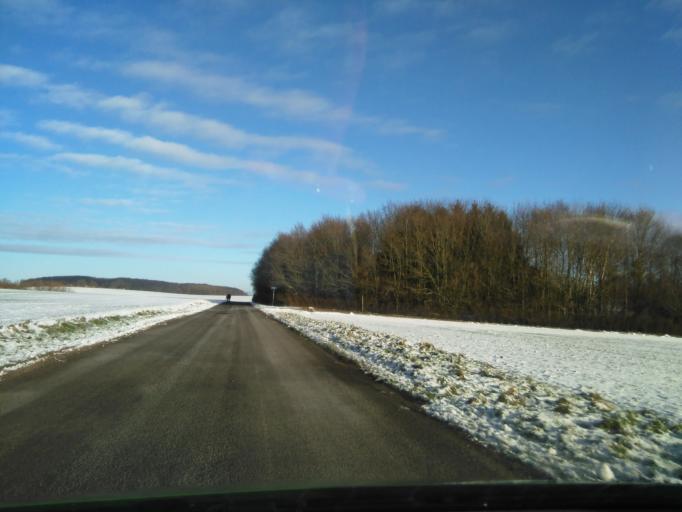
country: DK
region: Central Jutland
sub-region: Skanderborg Kommune
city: Skovby
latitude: 56.1391
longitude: 9.9459
